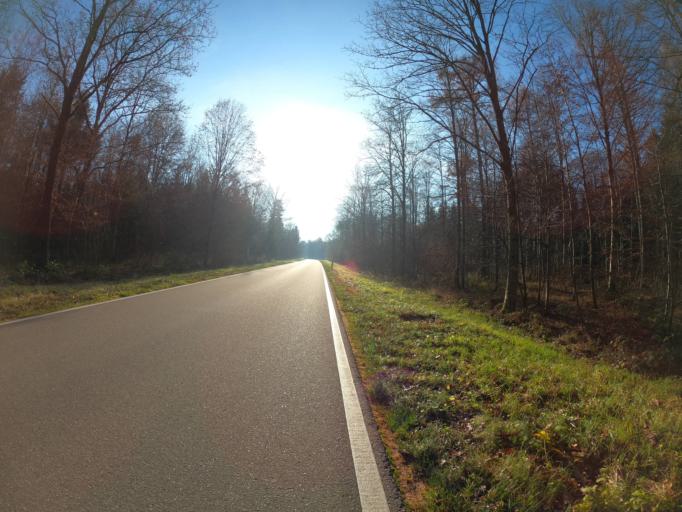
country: DE
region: Baden-Wuerttemberg
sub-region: Regierungsbezirk Stuttgart
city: Ebersbach an der Fils
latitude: 48.6942
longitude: 9.5379
